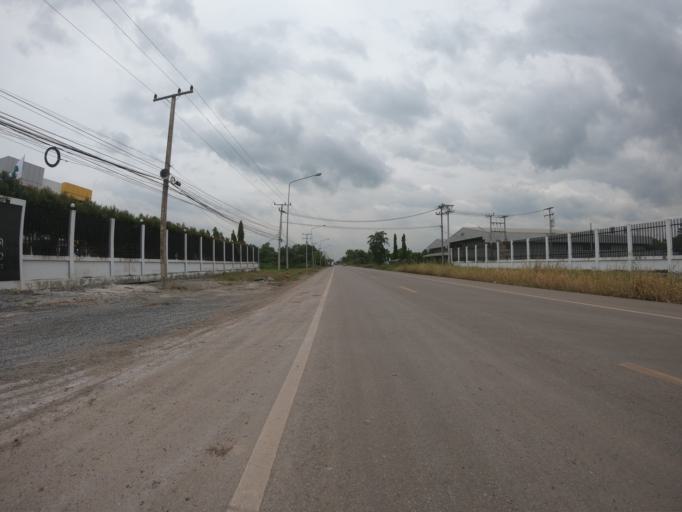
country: TH
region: Pathum Thani
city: Nong Suea
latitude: 14.0455
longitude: 100.8704
